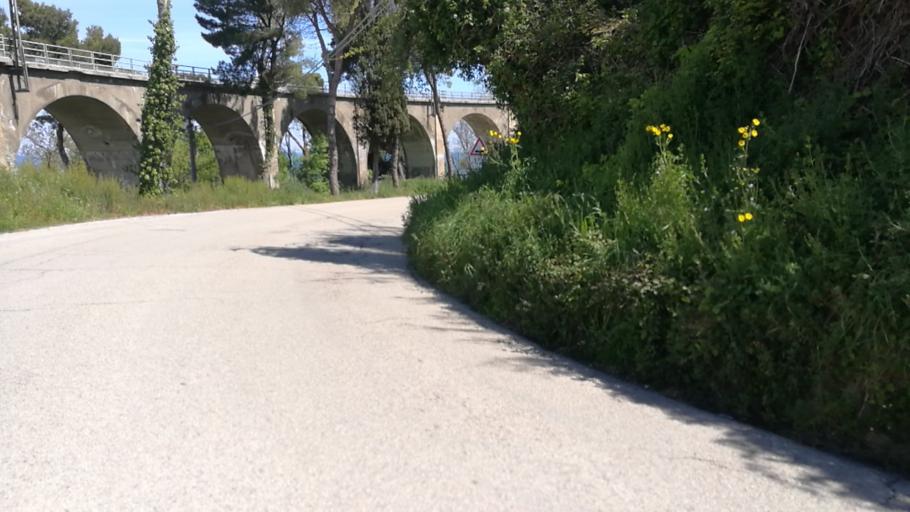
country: IT
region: Abruzzo
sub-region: Provincia di Chieti
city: Marina di San Vito
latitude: 42.3044
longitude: 14.4453
